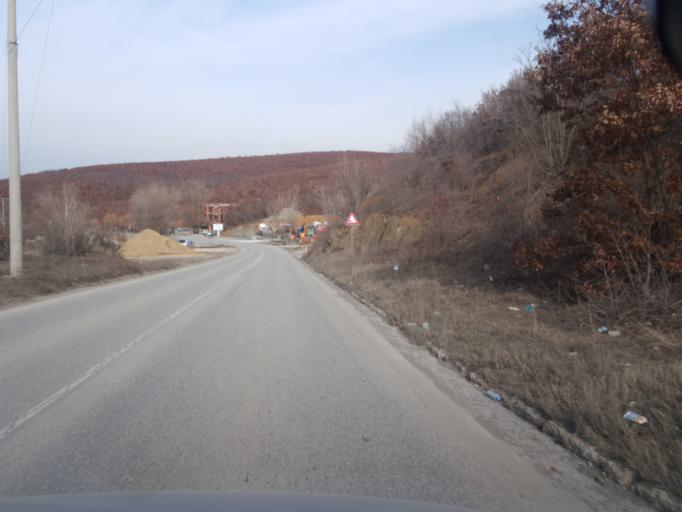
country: XK
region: Pec
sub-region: Komuna e Klines
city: Klina
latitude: 42.5603
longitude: 20.5686
